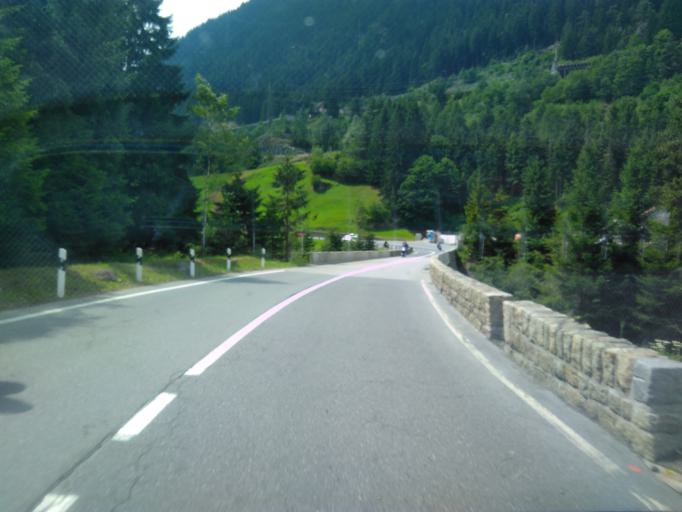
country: CH
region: Uri
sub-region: Uri
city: Andermatt
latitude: 46.6833
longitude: 8.5944
